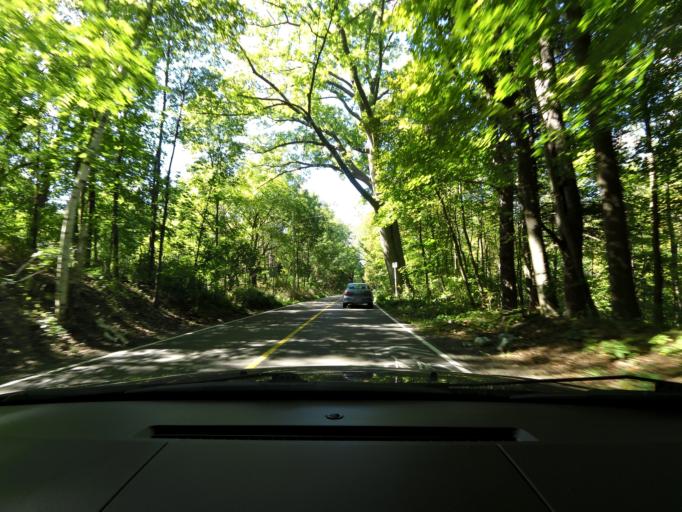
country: CA
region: Ontario
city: Hamilton
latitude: 43.3044
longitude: -79.8423
